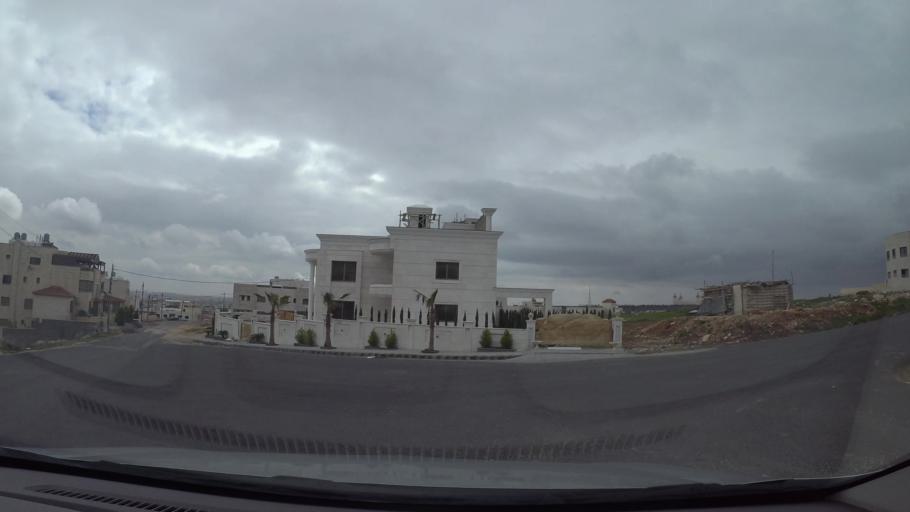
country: JO
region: Amman
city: Al Jubayhah
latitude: 31.9925
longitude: 35.8359
